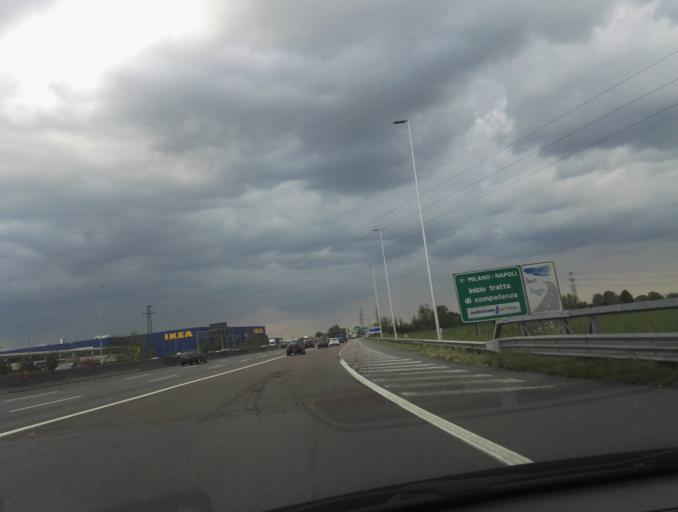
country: IT
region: Lombardy
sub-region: Citta metropolitana di Milano
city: Civesio
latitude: 45.3871
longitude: 9.2659
